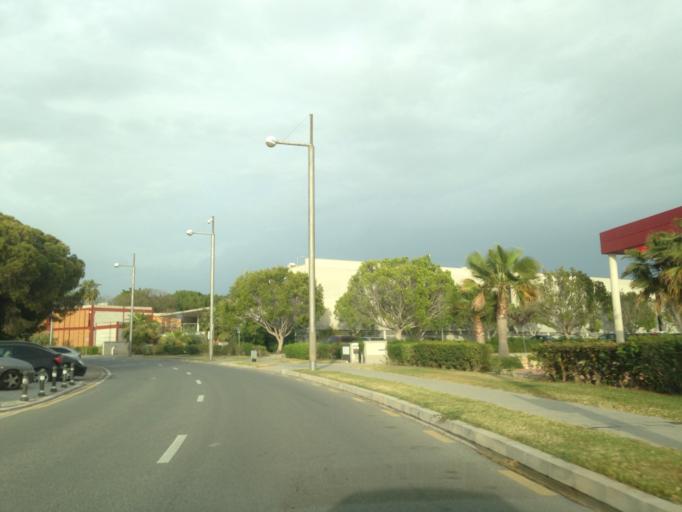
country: ES
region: Andalusia
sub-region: Provincia de Malaga
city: Estacion de Cartama
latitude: 36.7341
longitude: -4.5557
